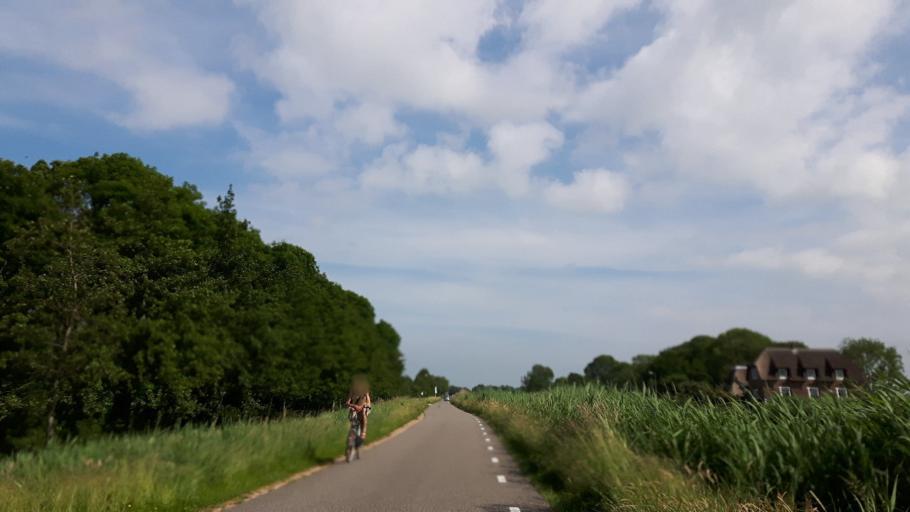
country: NL
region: Utrecht
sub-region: Gemeente De Ronde Venen
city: Mijdrecht
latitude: 52.1781
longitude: 4.8577
